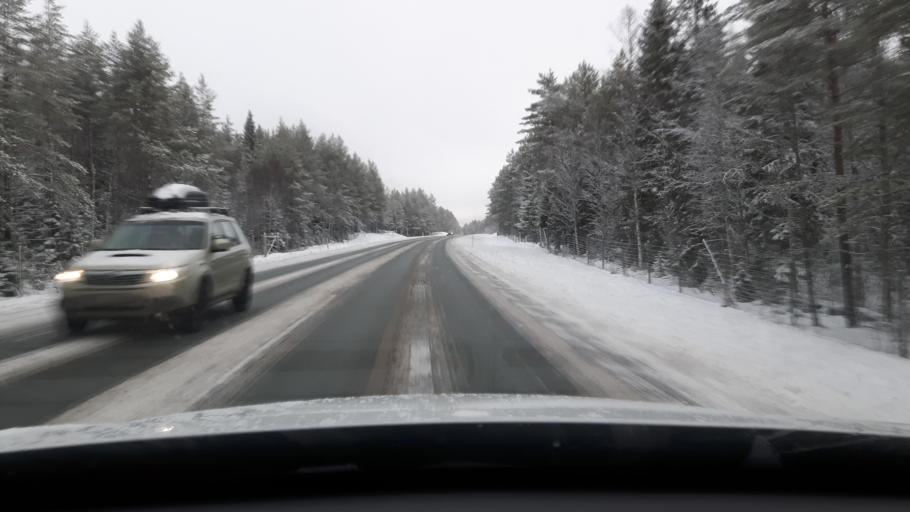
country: SE
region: Vaesterbotten
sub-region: Robertsfors Kommun
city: Robertsfors
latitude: 64.0359
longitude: 20.8427
